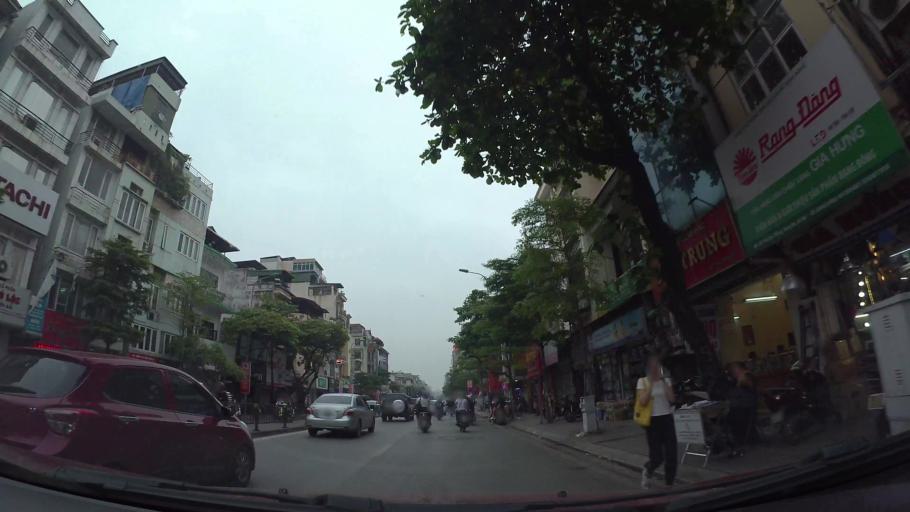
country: VN
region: Ha Noi
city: Dong Da
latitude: 21.0195
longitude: 105.8305
